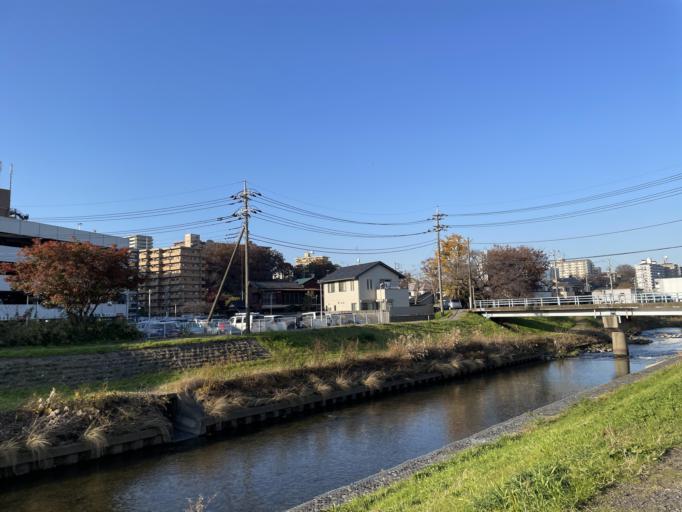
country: JP
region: Saitama
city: Asaka
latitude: 35.7993
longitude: 139.5808
